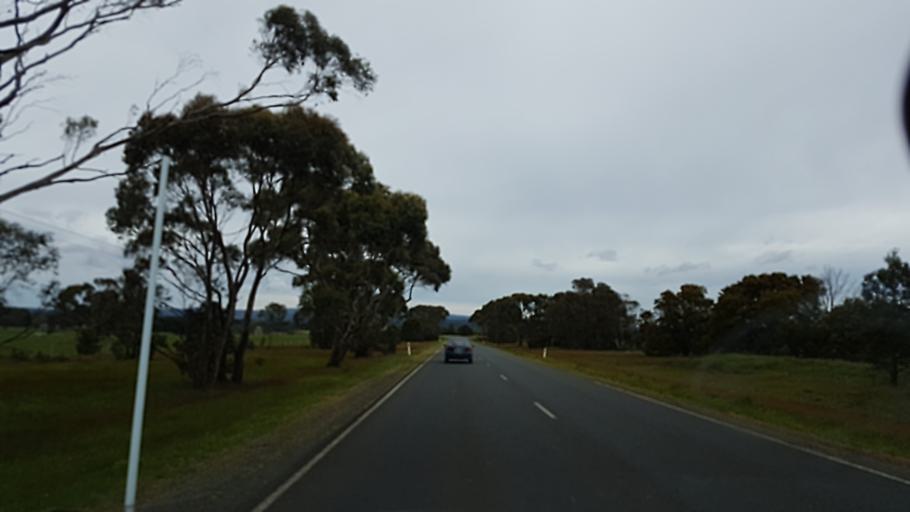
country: AU
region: Victoria
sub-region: Moorabool
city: Bacchus Marsh
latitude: -37.6190
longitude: 144.2117
